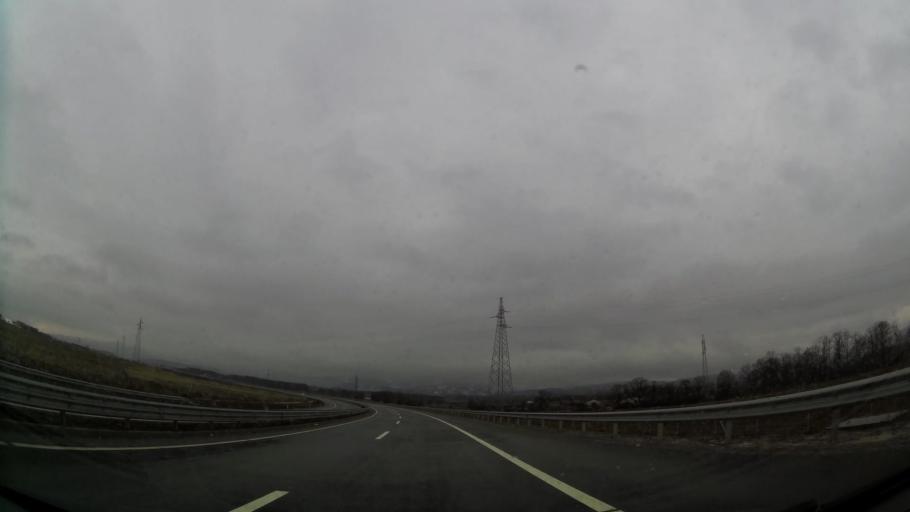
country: XK
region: Ferizaj
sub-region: Komuna e Ferizajt
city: Ferizaj
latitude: 42.3008
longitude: 21.2053
